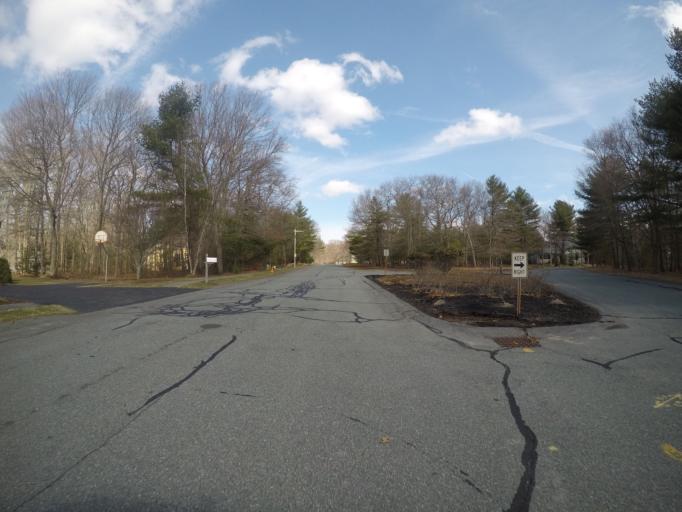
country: US
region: Massachusetts
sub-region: Bristol County
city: Easton
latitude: 42.0133
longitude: -71.1430
